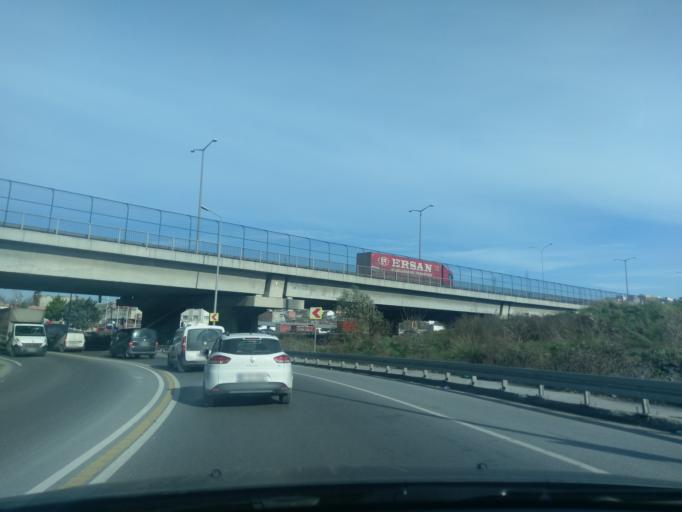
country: TR
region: Istanbul
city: Basaksehir
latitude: 41.0614
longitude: 28.7411
